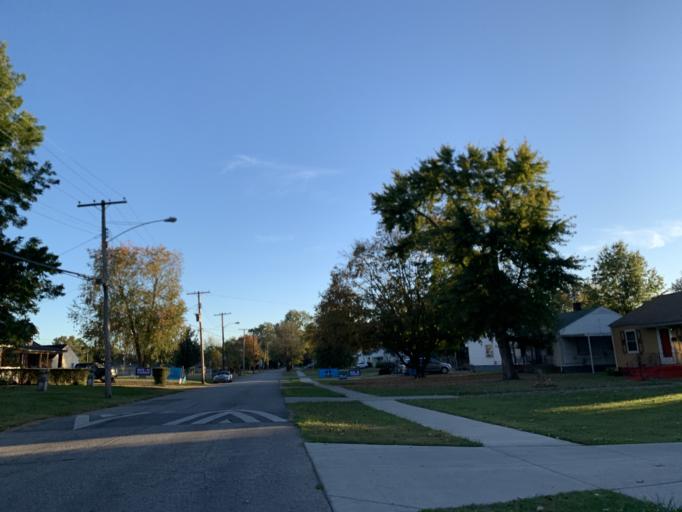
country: US
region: Indiana
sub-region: Floyd County
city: New Albany
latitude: 38.2469
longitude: -85.8274
